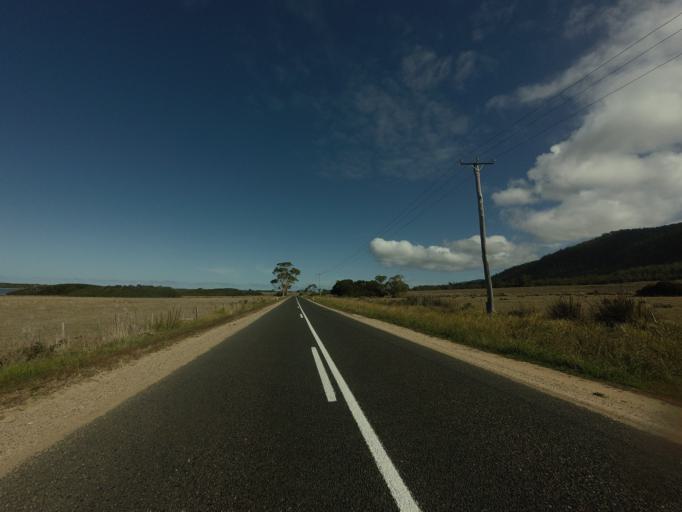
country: AU
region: Tasmania
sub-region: Break O'Day
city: St Helens
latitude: -41.7252
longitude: 148.2737
